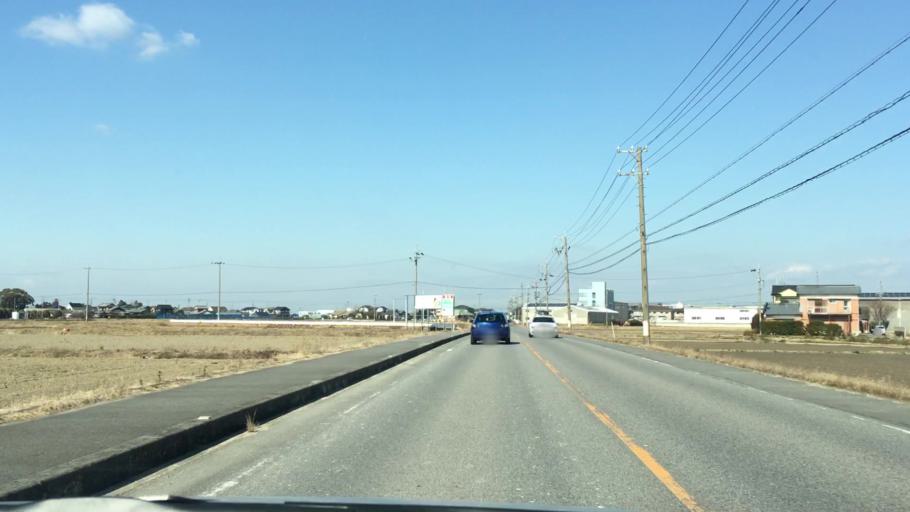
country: JP
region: Aichi
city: Anjo
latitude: 34.9834
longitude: 137.1180
